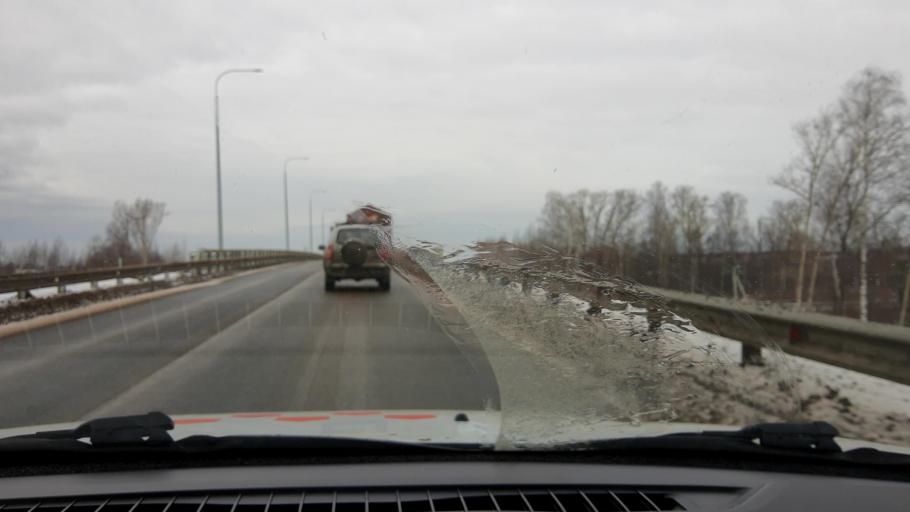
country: RU
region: Nizjnij Novgorod
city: Neklyudovo
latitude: 56.4231
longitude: 43.9846
